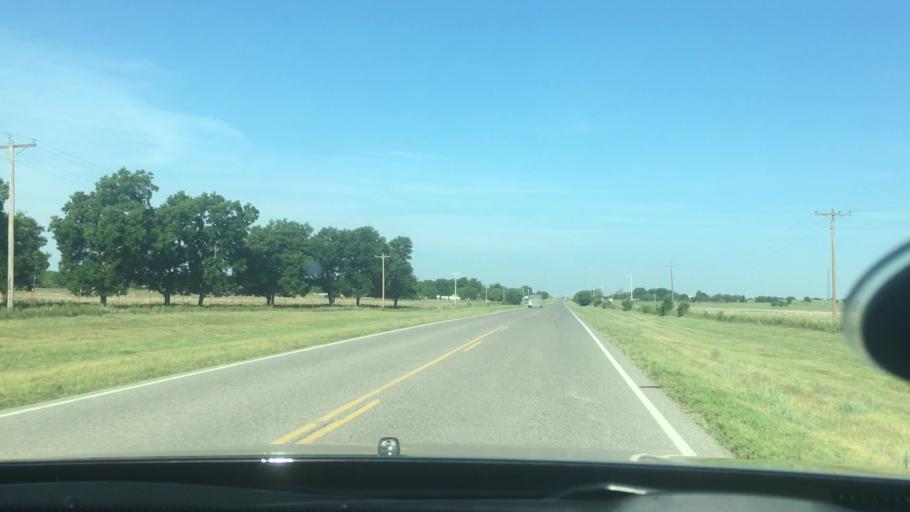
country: US
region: Oklahoma
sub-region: Garvin County
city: Wynnewood
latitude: 34.6518
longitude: -97.2312
